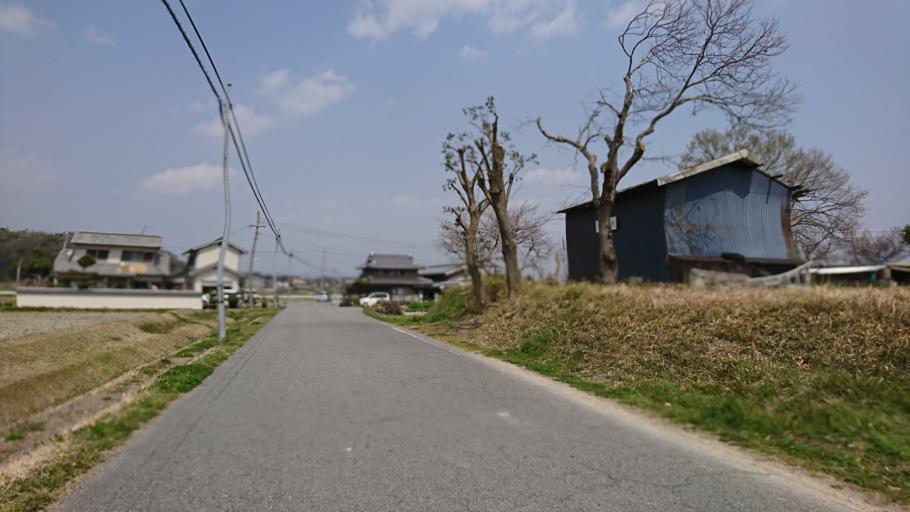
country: JP
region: Hyogo
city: Ono
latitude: 34.8339
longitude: 134.9055
